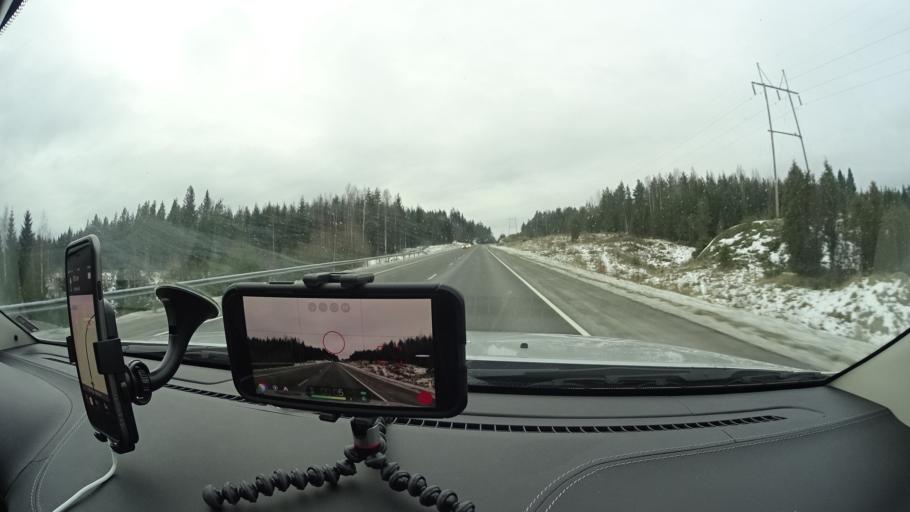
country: FI
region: Paijanne Tavastia
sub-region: Lahti
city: Heinola
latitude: 61.3035
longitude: 26.0560
